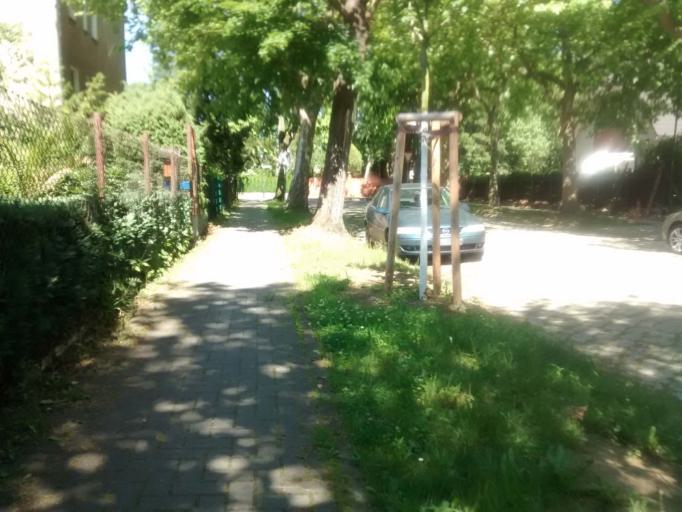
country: DE
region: Brandenburg
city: Hohen Neuendorf
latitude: 52.6745
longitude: 13.2700
